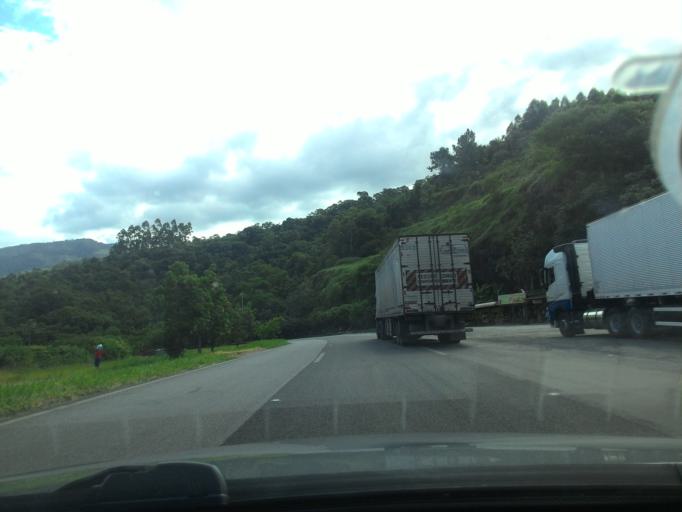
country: BR
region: Sao Paulo
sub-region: Cajati
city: Cajati
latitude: -24.7944
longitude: -48.2131
